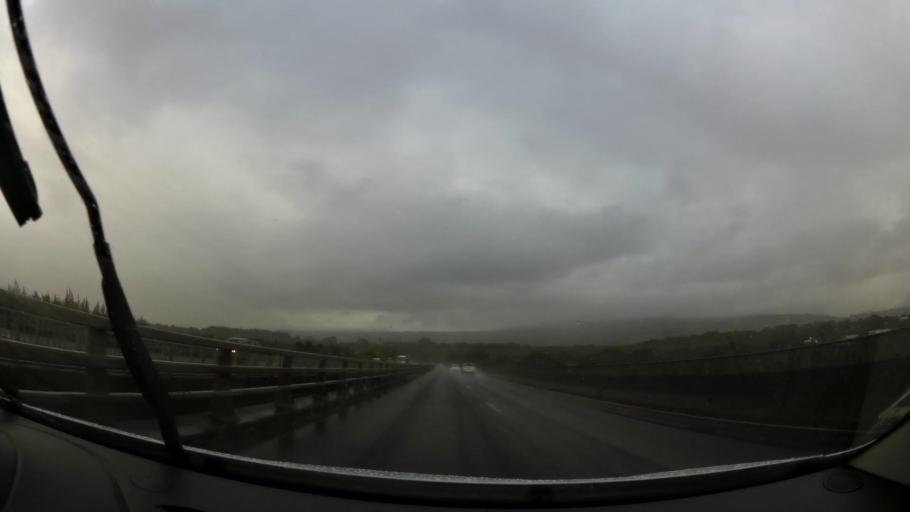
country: RE
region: Reunion
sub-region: Reunion
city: Saint-Andre
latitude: -20.9784
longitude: 55.6541
